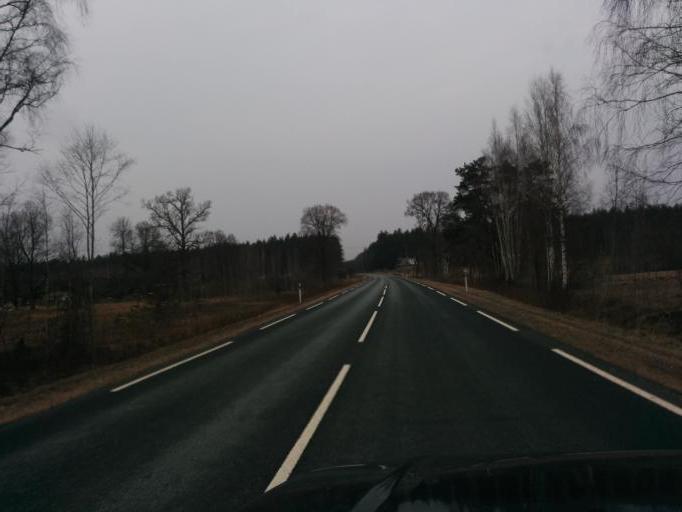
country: LV
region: Ogre
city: Ogre
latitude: 56.7895
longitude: 24.6068
